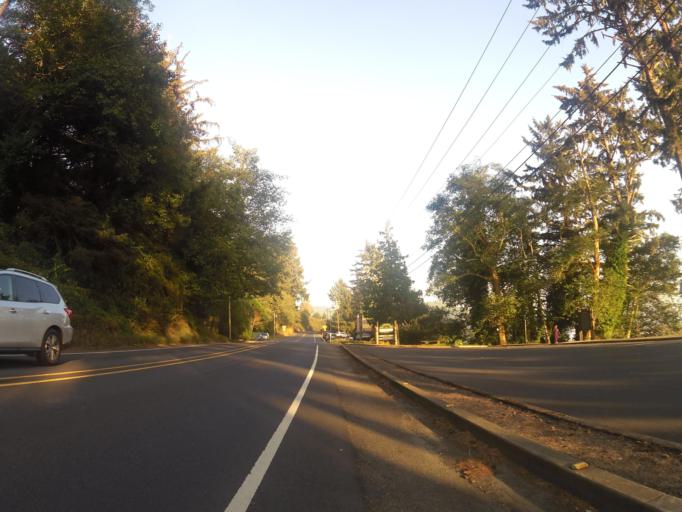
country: US
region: Oregon
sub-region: Tillamook County
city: Rockaway Beach
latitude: 45.5599
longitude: -123.9301
